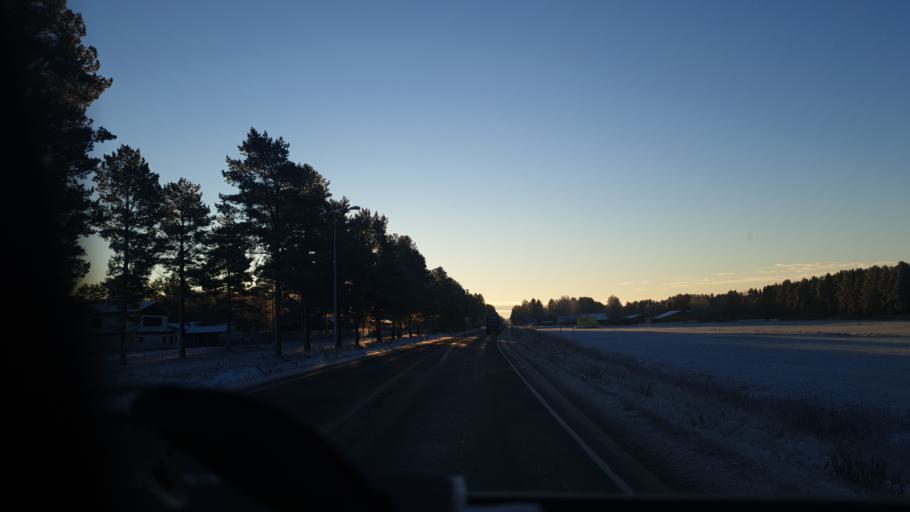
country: FI
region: Northern Ostrobothnia
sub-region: Ylivieska
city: Kalajoki
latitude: 64.2826
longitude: 23.9483
